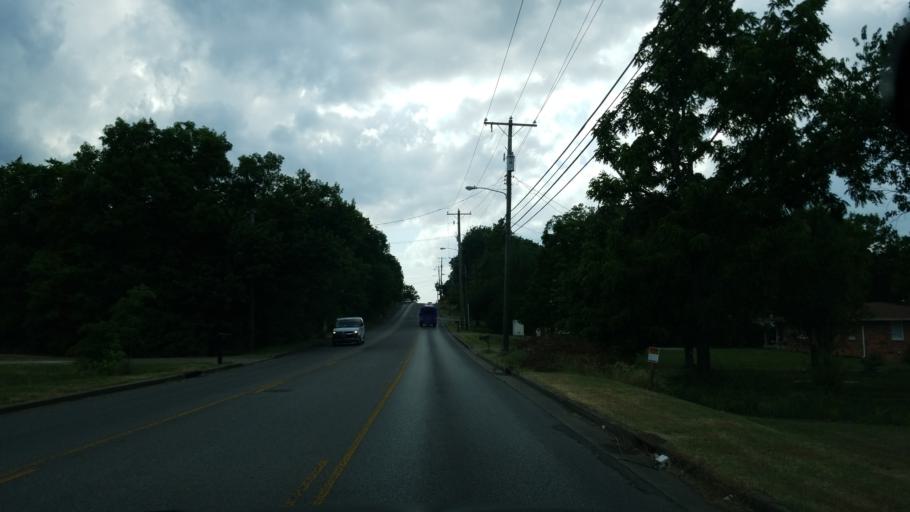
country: US
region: Tennessee
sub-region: Rutherford County
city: La Vergne
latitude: 36.0728
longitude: -86.6127
